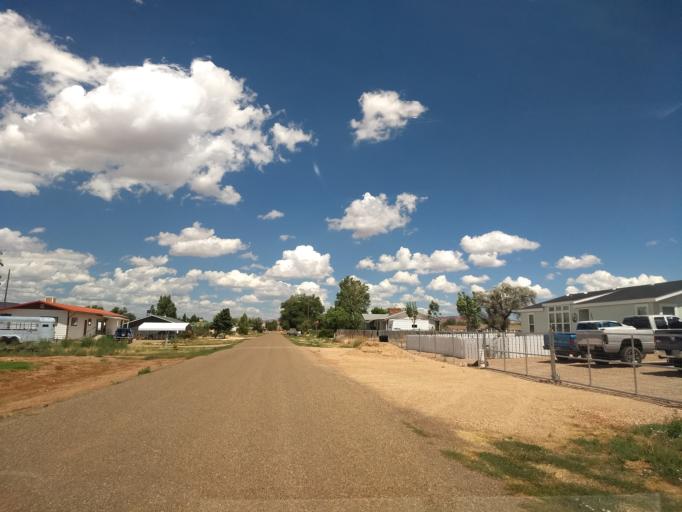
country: US
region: Arizona
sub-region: Coconino County
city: Fredonia
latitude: 36.9423
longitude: -112.5205
